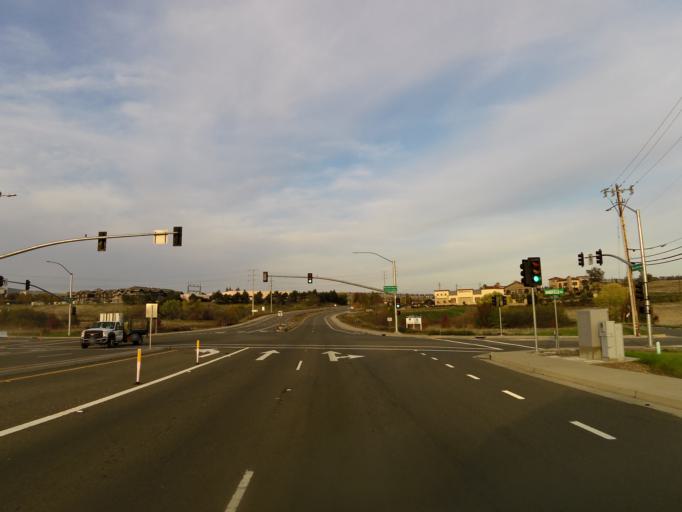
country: US
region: California
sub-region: El Dorado County
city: El Dorado Hills
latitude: 38.6436
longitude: -121.0715
